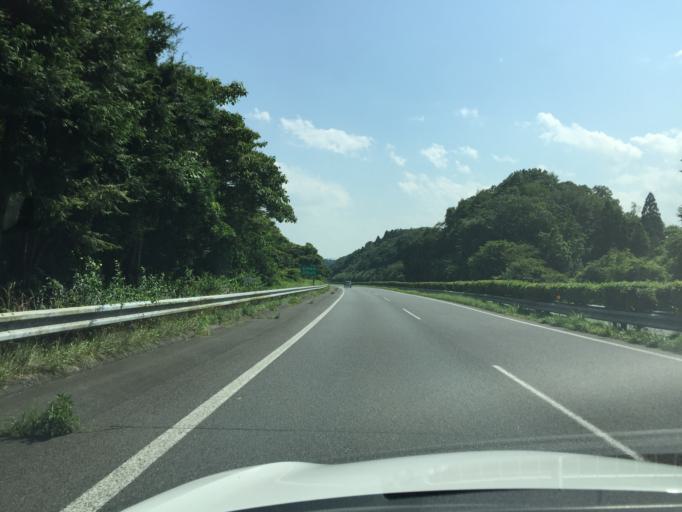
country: JP
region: Fukushima
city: Iwaki
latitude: 36.9620
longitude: 140.7826
